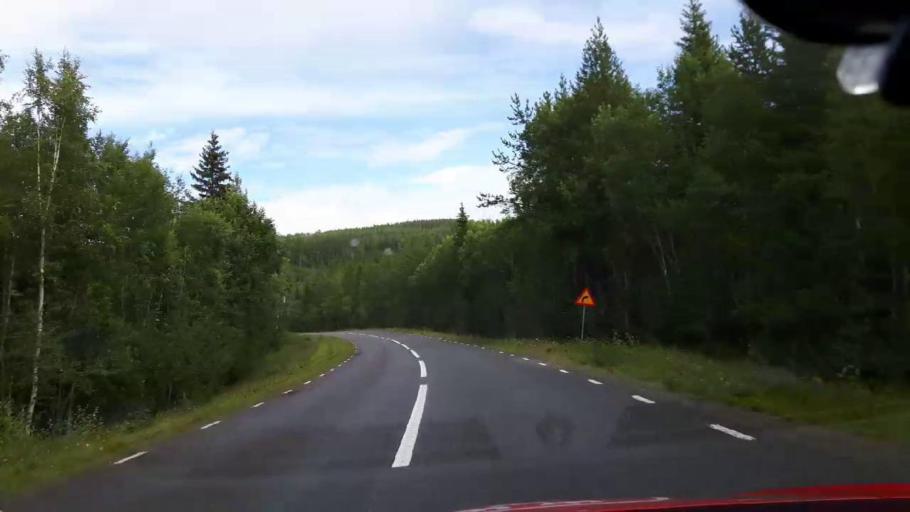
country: SE
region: Jaemtland
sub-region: Stroemsunds Kommun
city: Stroemsund
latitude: 64.3411
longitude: 14.9376
